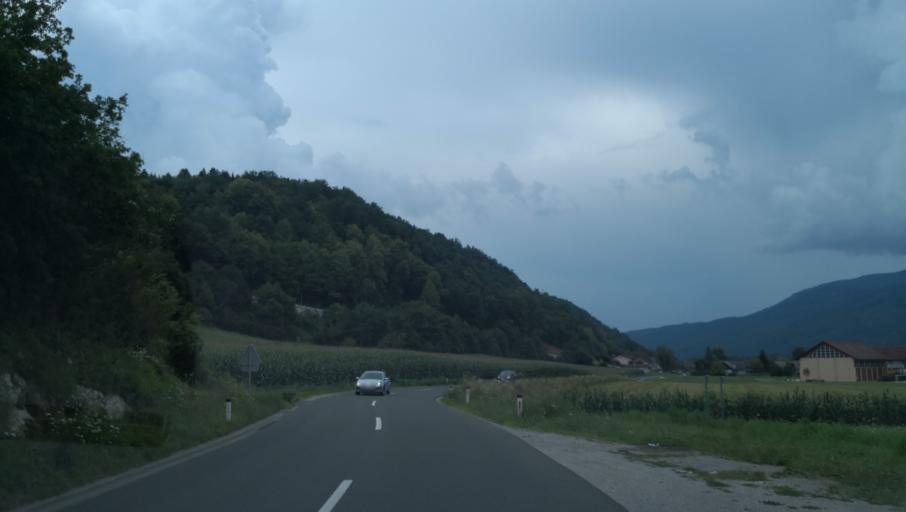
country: SI
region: Zuzemberk
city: Zuzemberk
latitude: 45.8145
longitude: 14.9628
